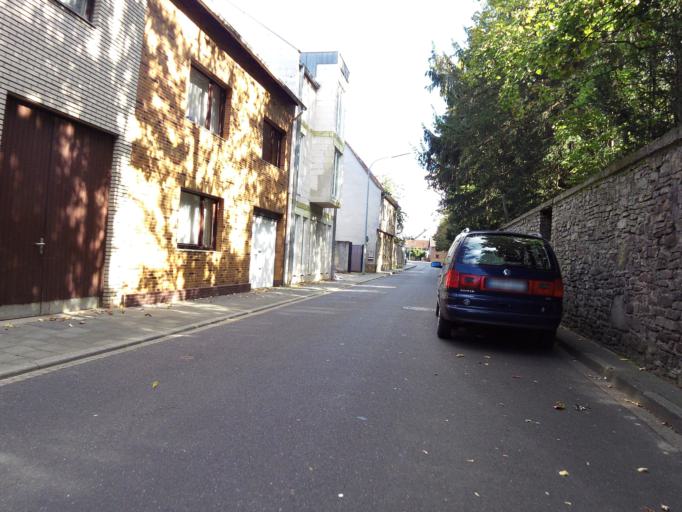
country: DE
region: North Rhine-Westphalia
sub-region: Regierungsbezirk Koln
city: Euskirchen
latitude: 50.6235
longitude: 6.8520
